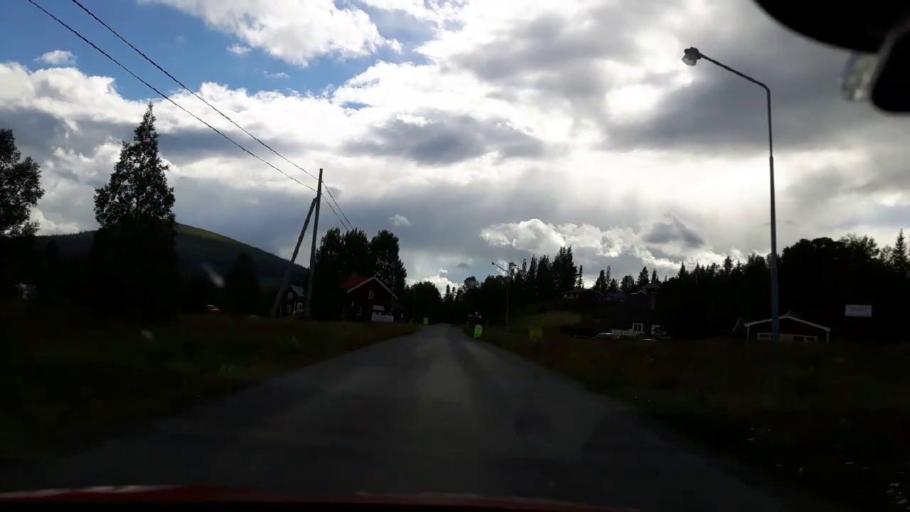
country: SE
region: Jaemtland
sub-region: Are Kommun
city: Are
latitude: 63.1668
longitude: 13.0608
